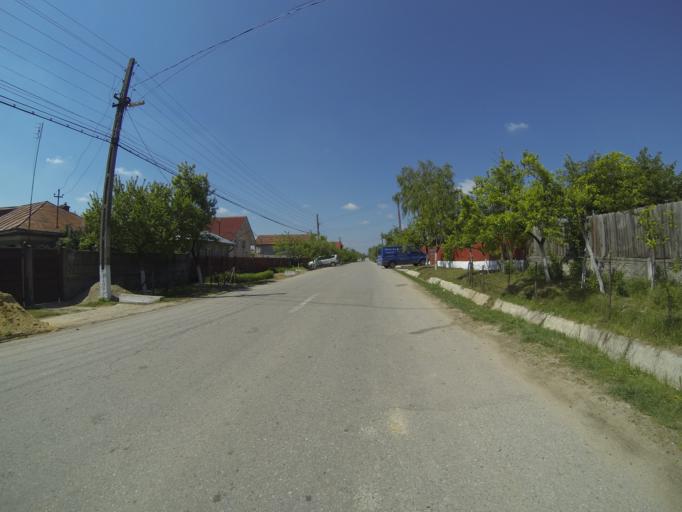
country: RO
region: Dolj
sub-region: Comuna Breasta
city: Breasta
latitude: 44.3001
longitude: 23.6567
